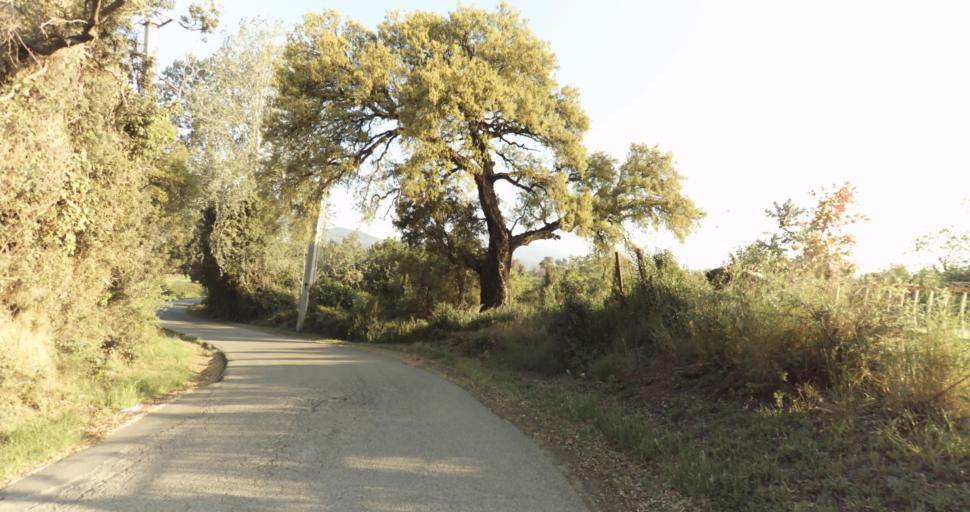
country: FR
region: Corsica
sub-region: Departement de la Haute-Corse
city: Biguglia
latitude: 42.6096
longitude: 9.4435
